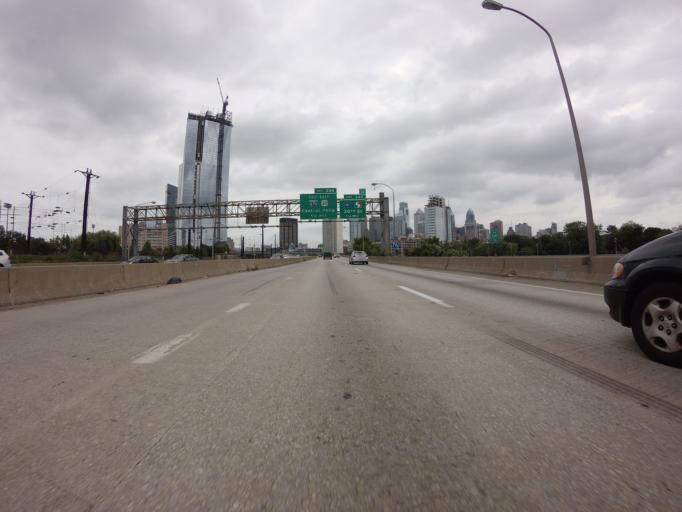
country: US
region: Pennsylvania
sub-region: Philadelphia County
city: Philadelphia
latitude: 39.9487
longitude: -75.1856
